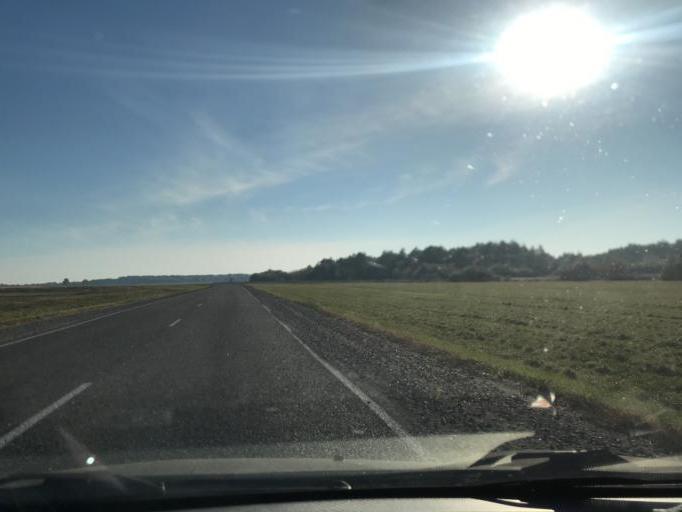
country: BY
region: Gomel
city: Brahin
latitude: 51.7733
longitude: 30.2698
